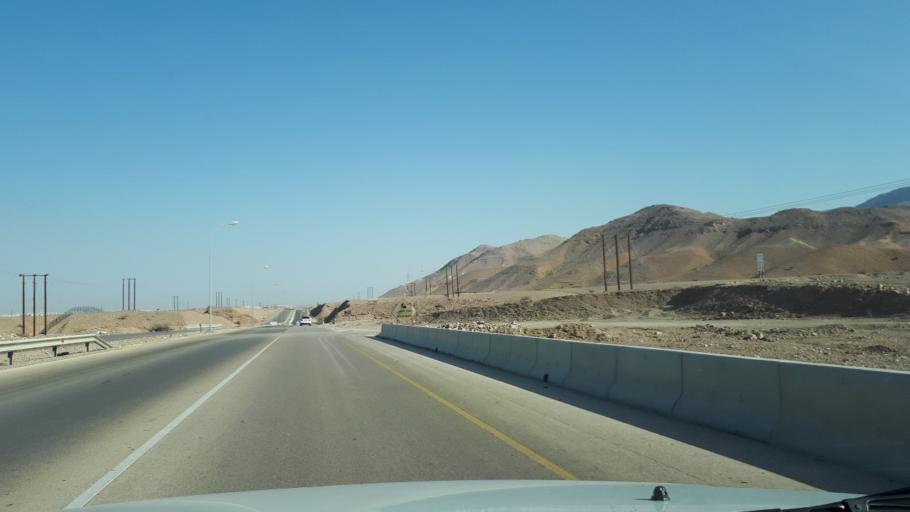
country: OM
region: Ash Sharqiyah
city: Sur
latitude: 22.6393
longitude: 59.4018
